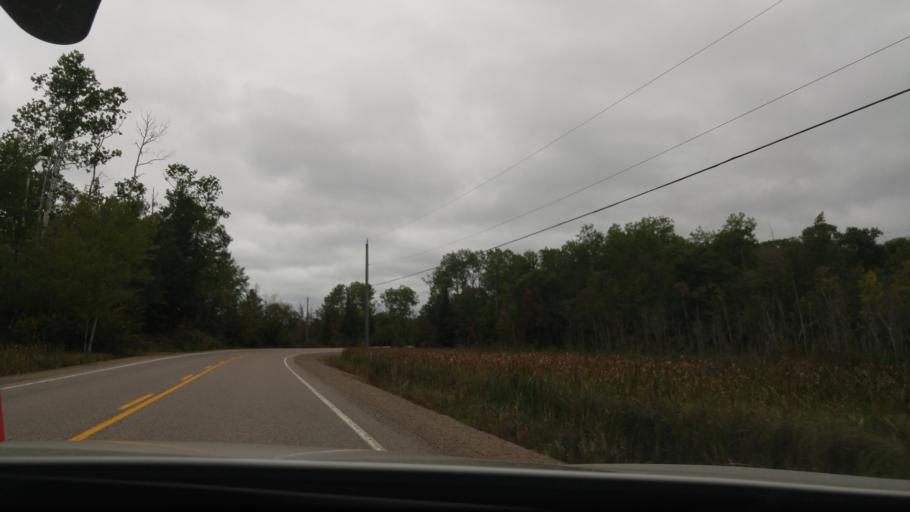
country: CA
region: Ontario
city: Petawawa
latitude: 45.8183
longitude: -77.3142
